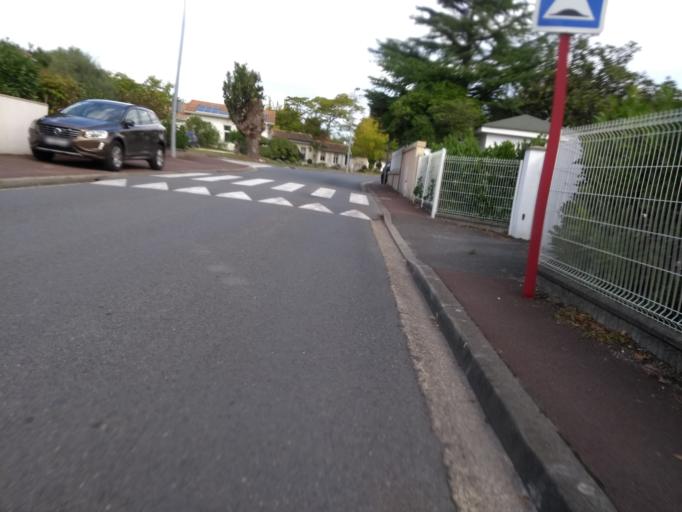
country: FR
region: Aquitaine
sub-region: Departement de la Gironde
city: Canejan
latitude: 44.7696
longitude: -0.6574
